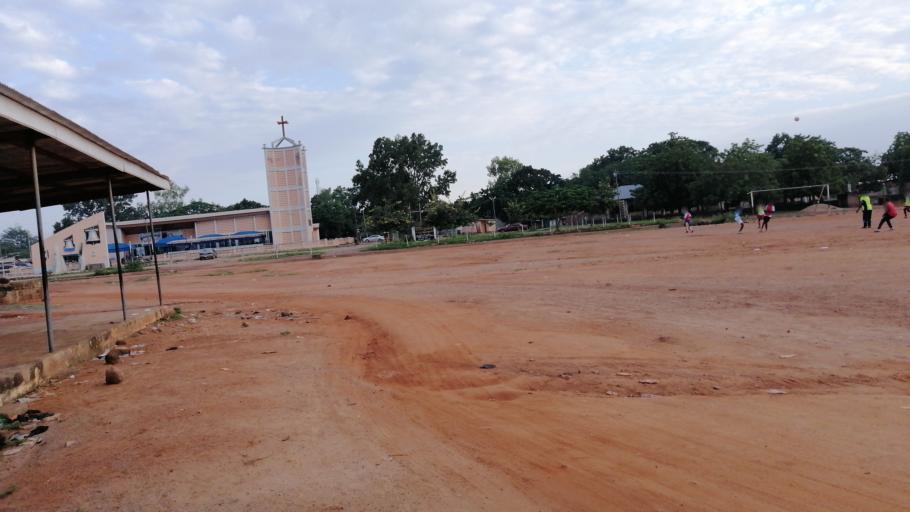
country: GH
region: Upper East
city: Bolgatanga
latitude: 10.7911
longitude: -0.8549
